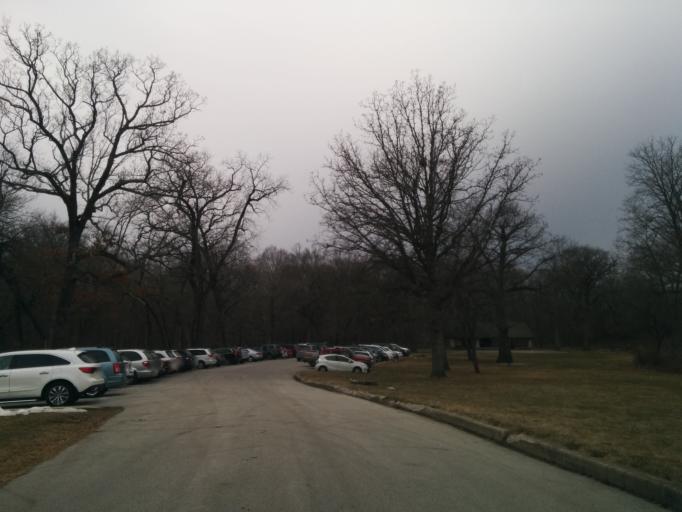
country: US
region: Illinois
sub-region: Cook County
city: Prospect Heights
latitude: 42.1008
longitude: -87.8855
